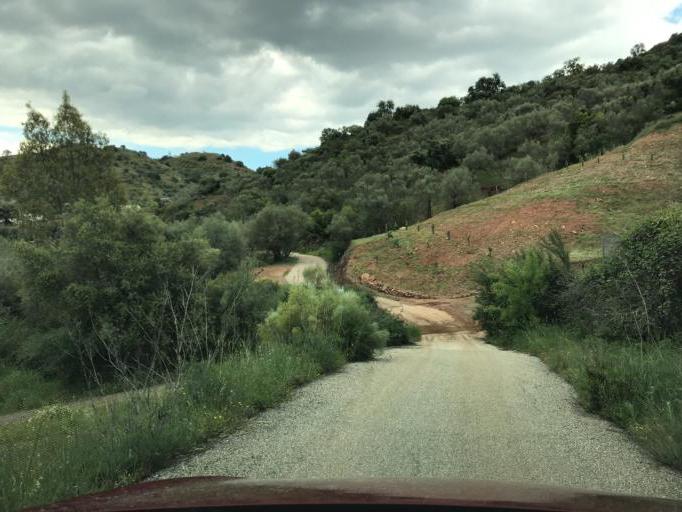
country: ES
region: Andalusia
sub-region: Provincia de Malaga
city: Comares
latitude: 36.8776
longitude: -4.2603
